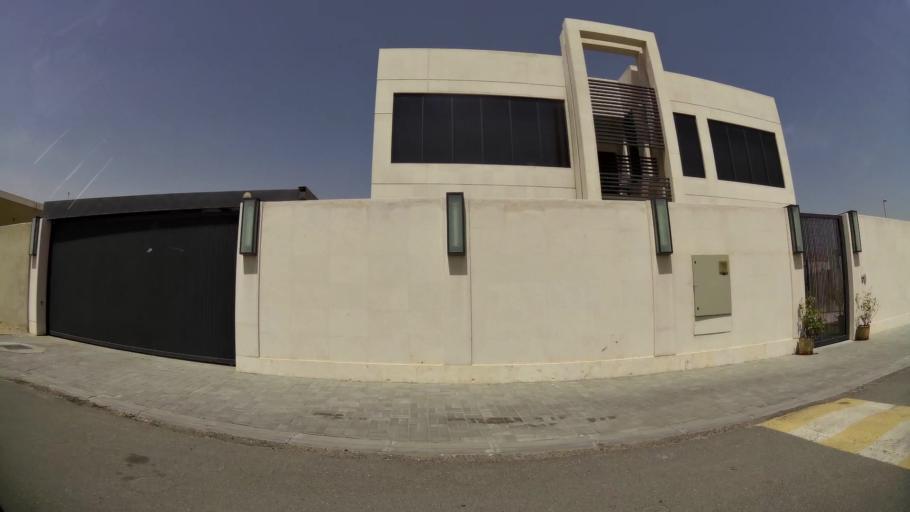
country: AE
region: Ash Shariqah
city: Sharjah
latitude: 25.1840
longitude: 55.4214
